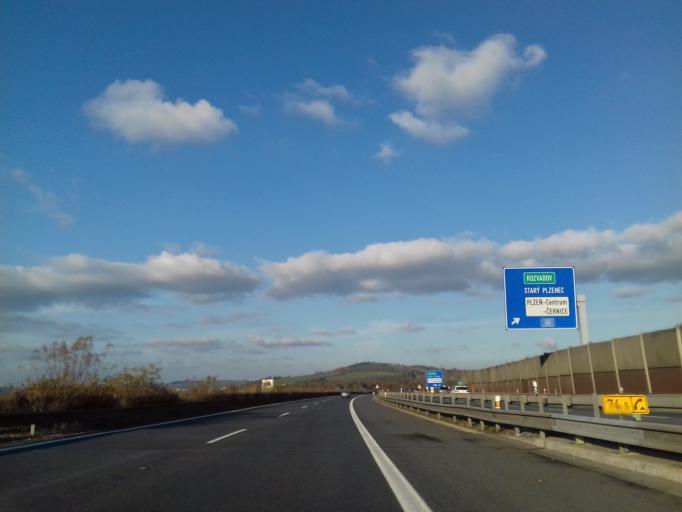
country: CZ
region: Plzensky
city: Stenovice
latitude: 49.6980
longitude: 13.4312
